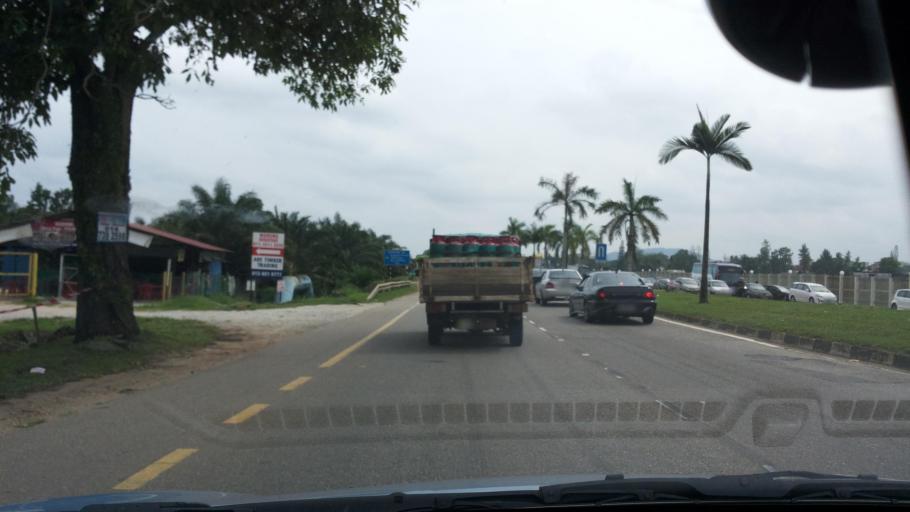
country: MY
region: Pahang
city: Kuantan
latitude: 3.7603
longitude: 103.2099
